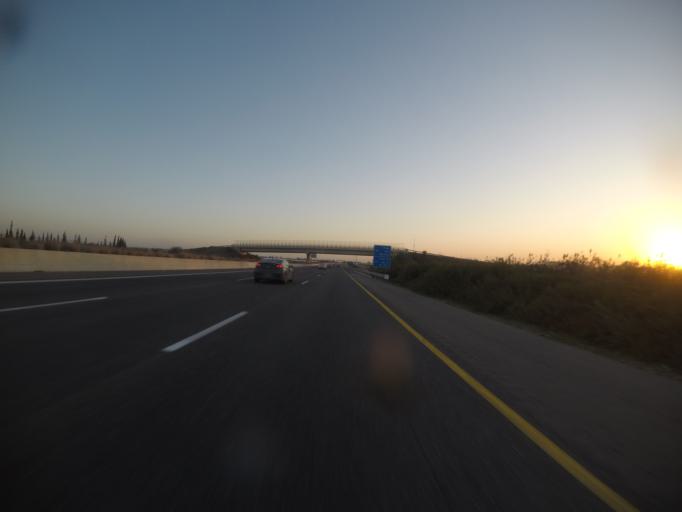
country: PS
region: West Bank
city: Zayta
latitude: 32.4017
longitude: 35.0203
